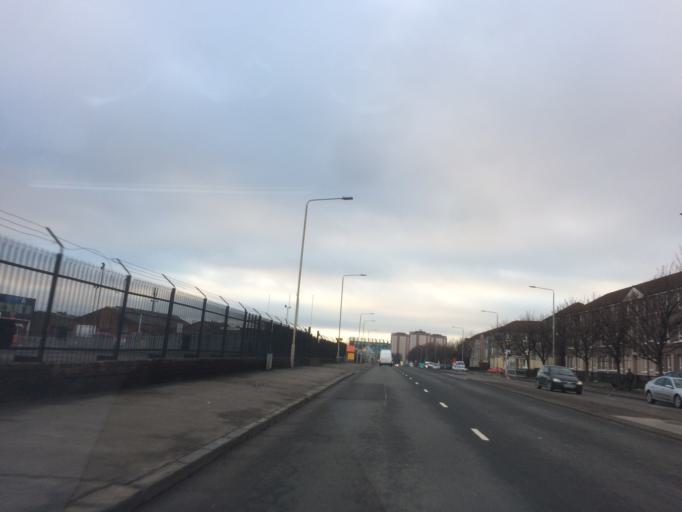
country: GB
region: Scotland
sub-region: South Lanarkshire
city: Rutherglen
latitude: 55.8429
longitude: -4.1900
